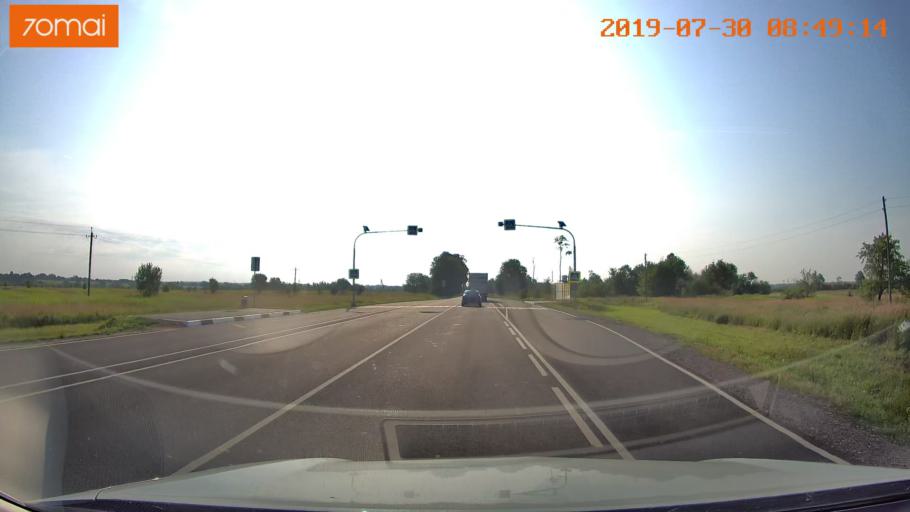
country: RU
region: Kaliningrad
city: Chernyakhovsk
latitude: 54.6141
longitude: 21.9182
